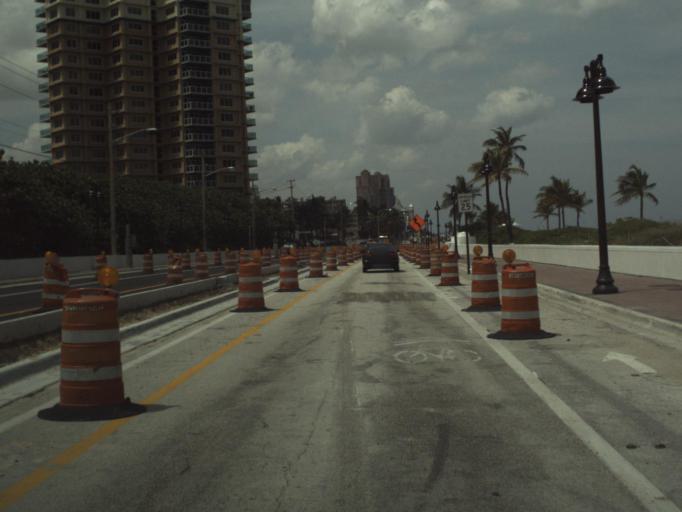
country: US
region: Florida
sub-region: Broward County
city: Sunrise
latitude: 26.1432
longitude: -80.1024
